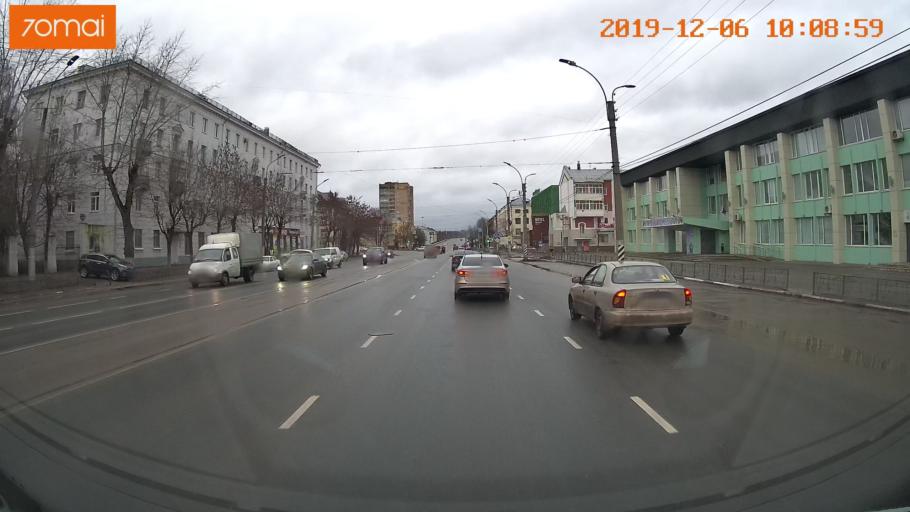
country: RU
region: Ivanovo
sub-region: Gorod Ivanovo
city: Ivanovo
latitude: 57.0195
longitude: 40.9687
